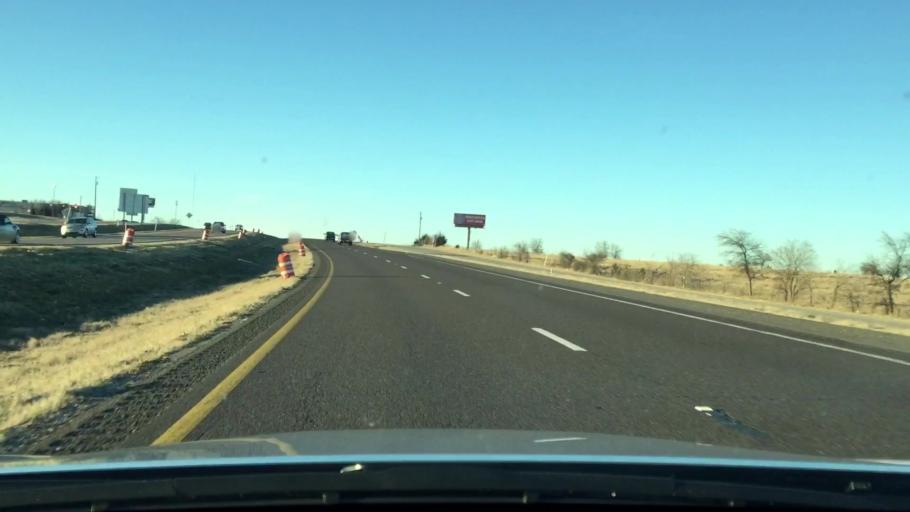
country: US
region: Texas
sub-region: Cooke County
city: Gainesville
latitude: 33.6732
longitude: -97.1514
